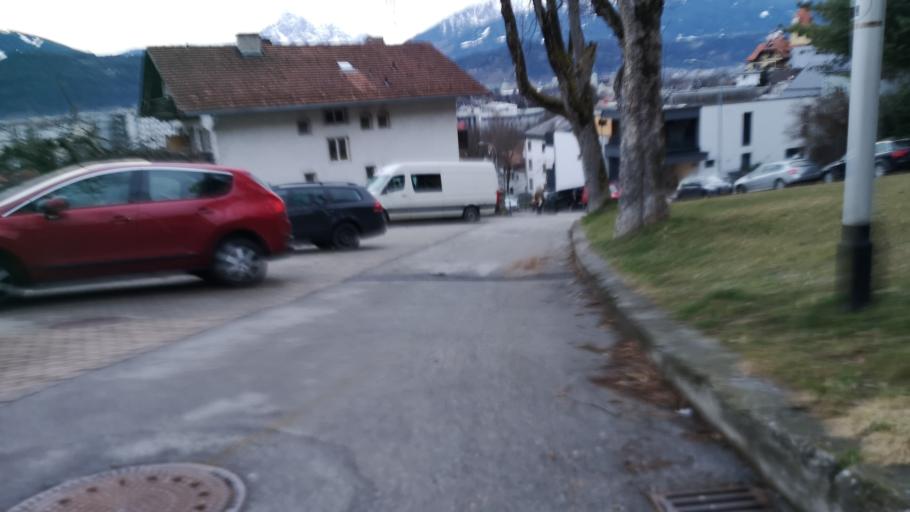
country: AT
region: Tyrol
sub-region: Innsbruck Stadt
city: Innsbruck
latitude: 47.2835
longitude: 11.4072
